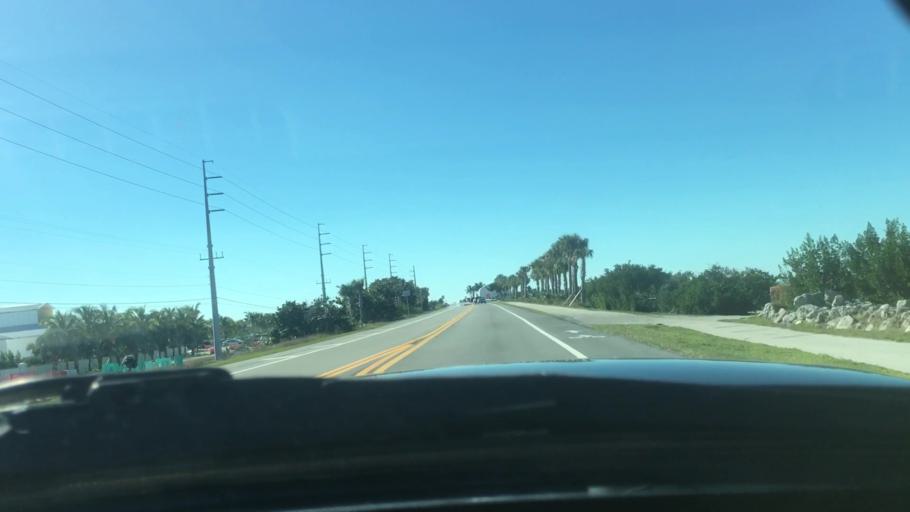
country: US
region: Florida
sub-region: Monroe County
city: Marathon
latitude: 24.7075
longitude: -81.1194
